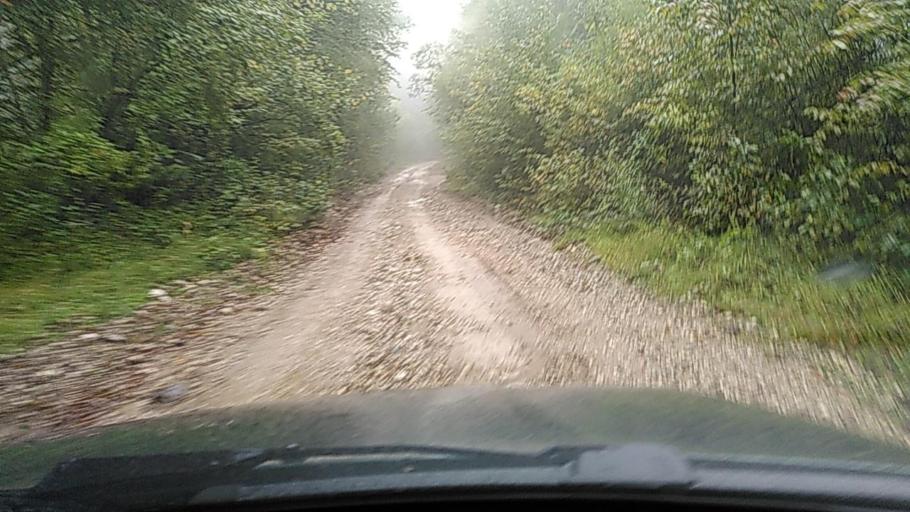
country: RU
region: Kabardino-Balkariya
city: Belaya Rechka
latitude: 43.3788
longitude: 43.4343
